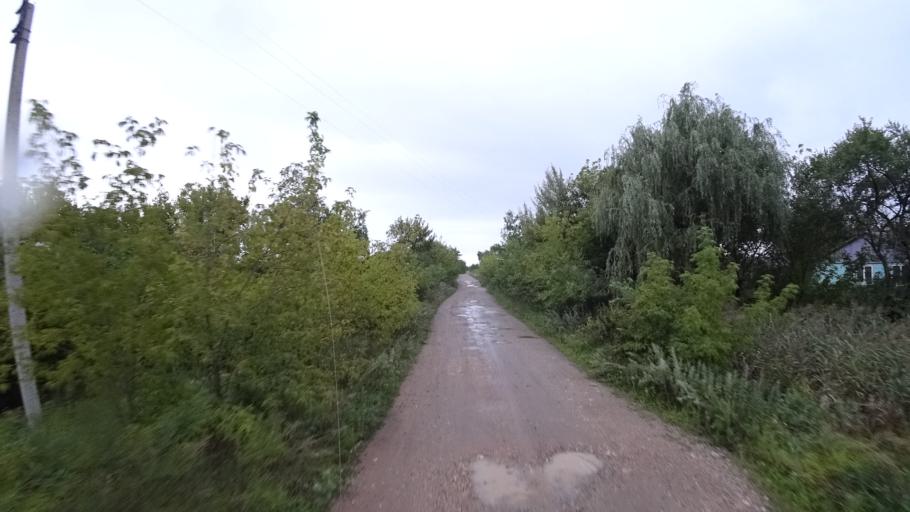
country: RU
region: Primorskiy
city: Chernigovka
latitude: 44.3989
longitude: 132.5295
